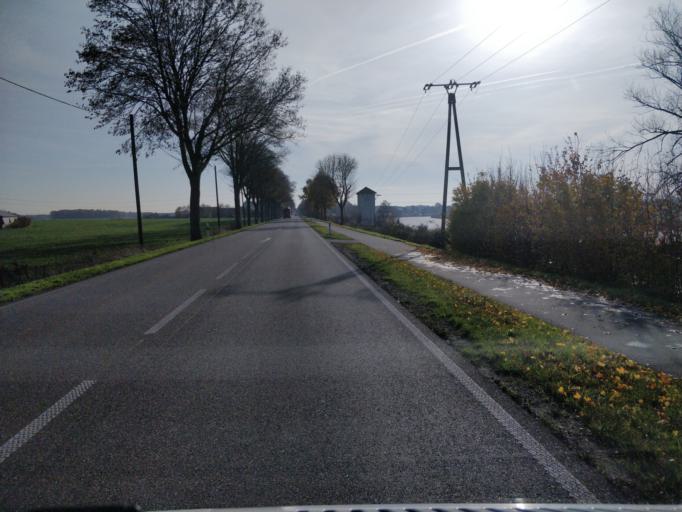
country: DE
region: North Rhine-Westphalia
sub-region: Regierungsbezirk Dusseldorf
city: Mehrhoog
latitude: 51.7525
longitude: 6.4863
